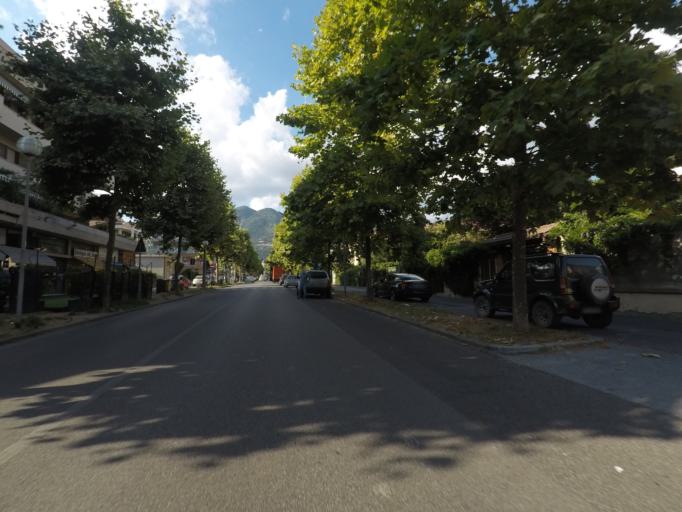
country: IT
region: Tuscany
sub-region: Provincia di Massa-Carrara
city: Massa
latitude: 44.0297
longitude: 10.1373
